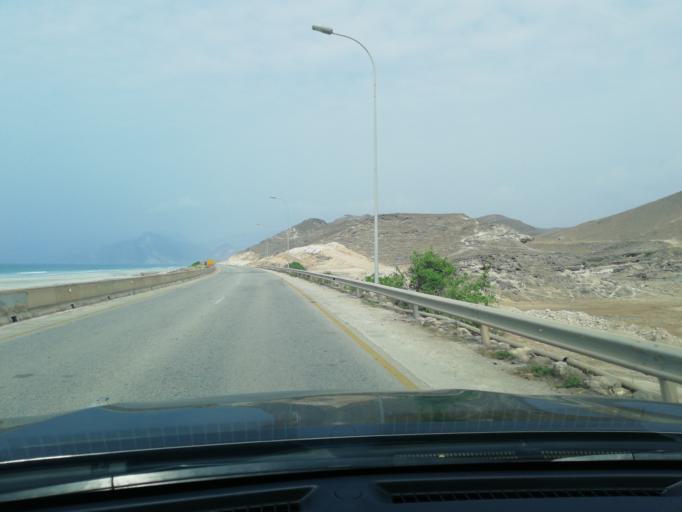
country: OM
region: Zufar
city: Salalah
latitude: 16.8865
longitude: 53.8137
